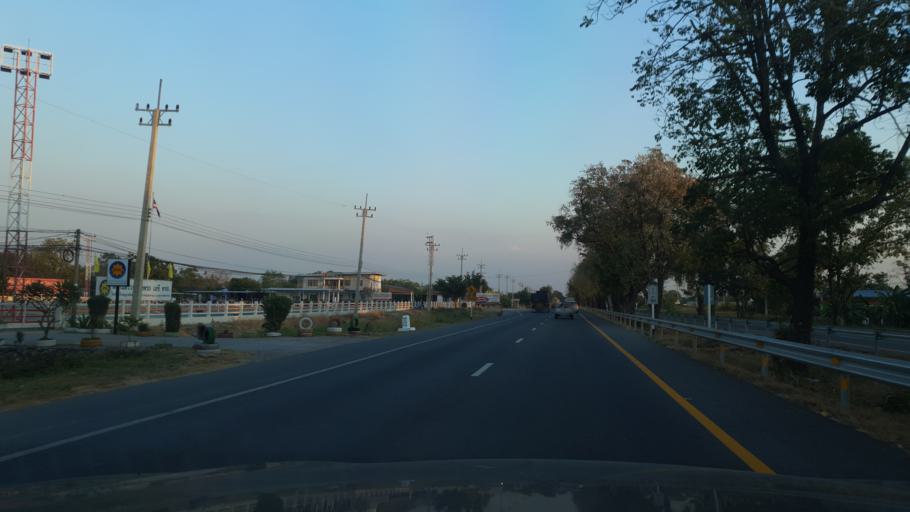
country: TH
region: Nakhon Sawan
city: Banphot Phisai
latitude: 15.8086
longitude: 99.9496
